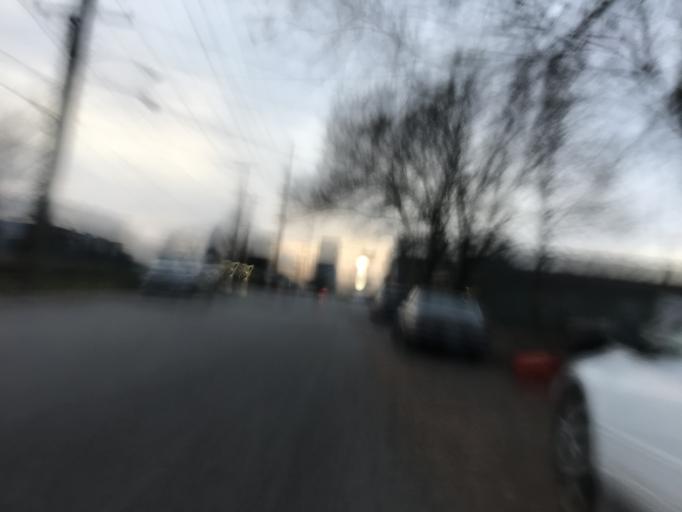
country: US
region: Indiana
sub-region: Clark County
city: Jeffersonville
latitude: 38.2563
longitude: -85.7367
